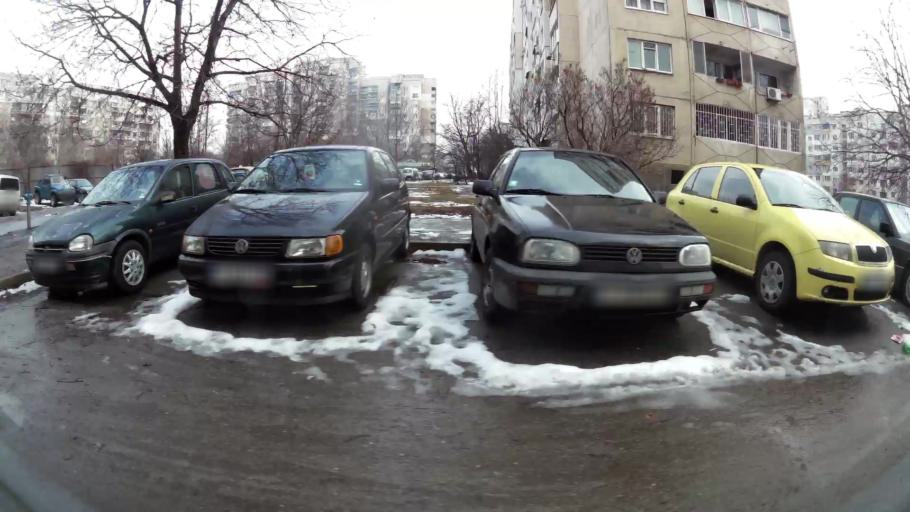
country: BG
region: Sofia-Capital
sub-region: Stolichna Obshtina
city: Sofia
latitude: 42.7108
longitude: 23.2656
